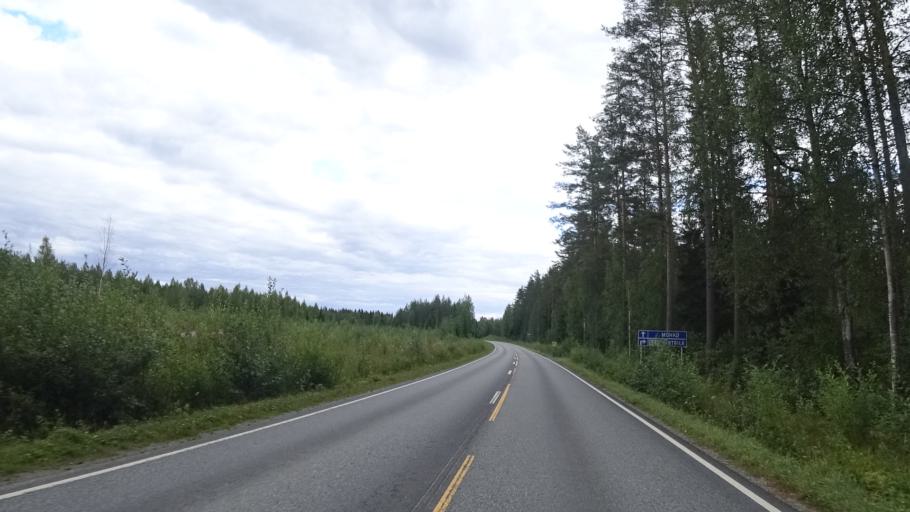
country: FI
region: North Karelia
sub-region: Joensuu
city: Ilomantsi
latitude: 62.6510
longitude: 30.9726
